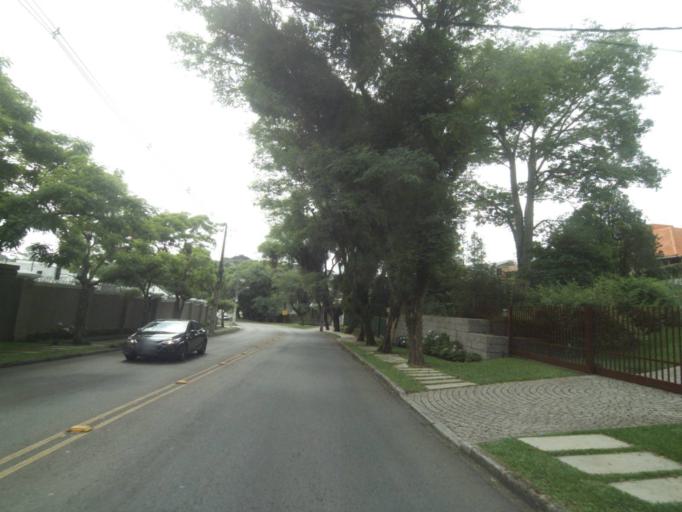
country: BR
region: Parana
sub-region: Curitiba
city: Curitiba
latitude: -25.4047
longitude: -49.3014
